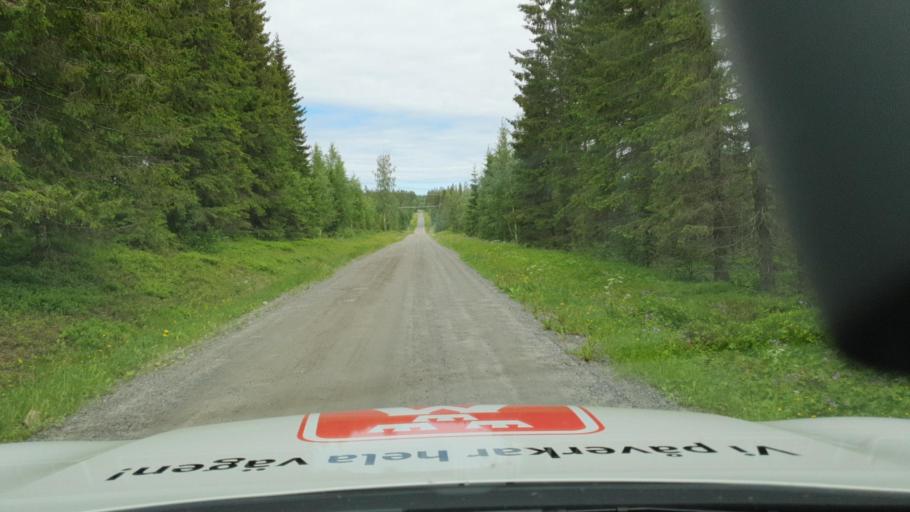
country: SE
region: Vaesterbotten
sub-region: Skelleftea Kommun
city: Langsele
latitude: 64.4683
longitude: 20.2691
